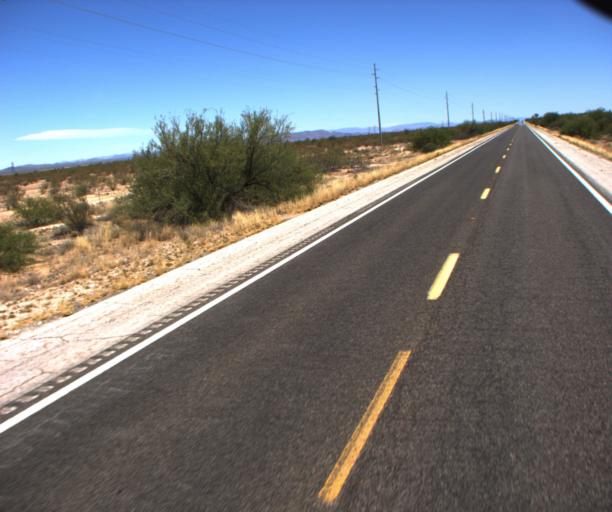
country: US
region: Arizona
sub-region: La Paz County
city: Salome
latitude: 33.8960
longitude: -113.3188
